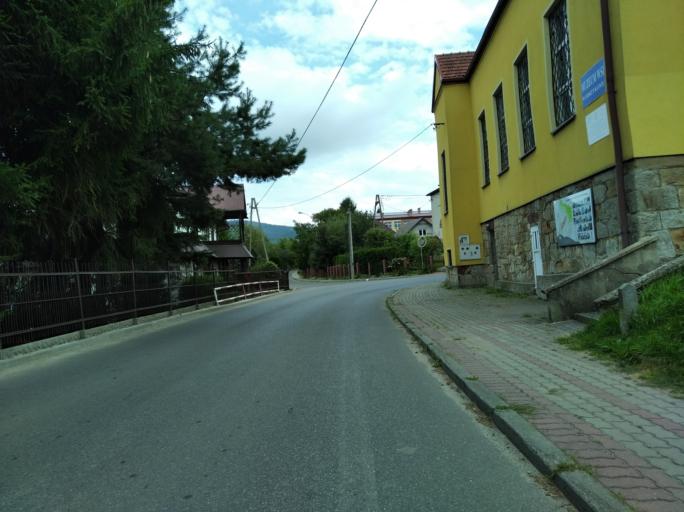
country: PL
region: Subcarpathian Voivodeship
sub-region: Powiat krosnienski
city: Odrzykon
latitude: 49.7405
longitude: 21.7428
